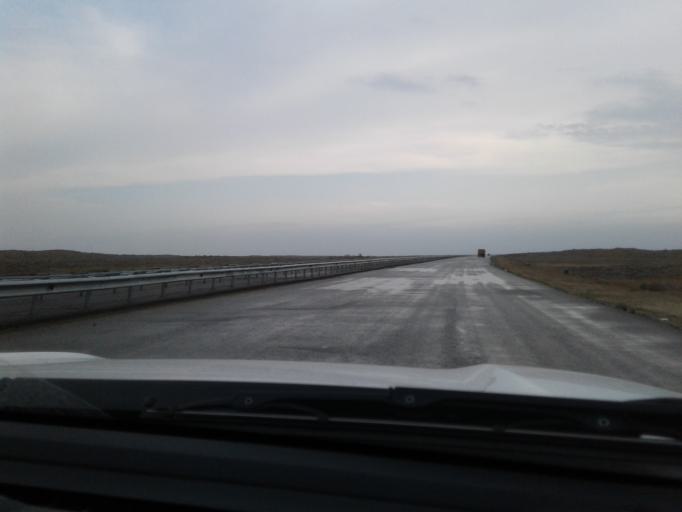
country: TM
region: Ahal
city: Abadan
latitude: 38.4702
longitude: 58.5056
